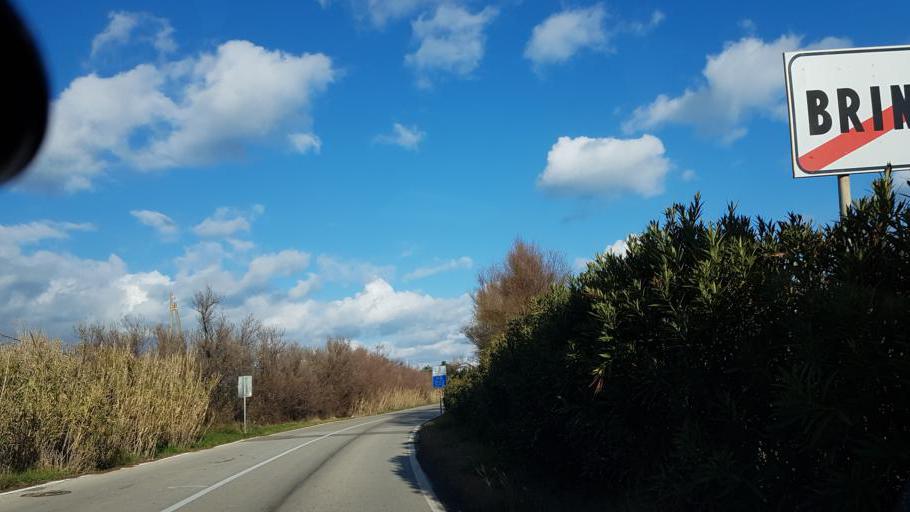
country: IT
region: Apulia
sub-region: Provincia di Brindisi
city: Materdomini
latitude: 40.6696
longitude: 17.9467
